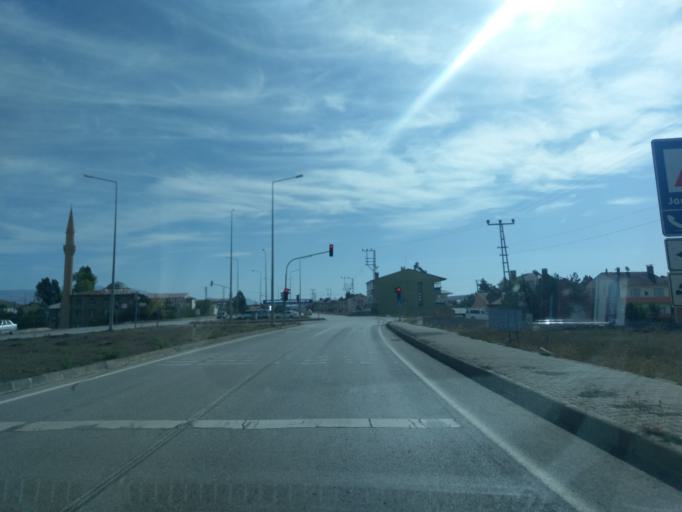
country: TR
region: Sivas
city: Imranli
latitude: 39.8716
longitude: 38.1103
